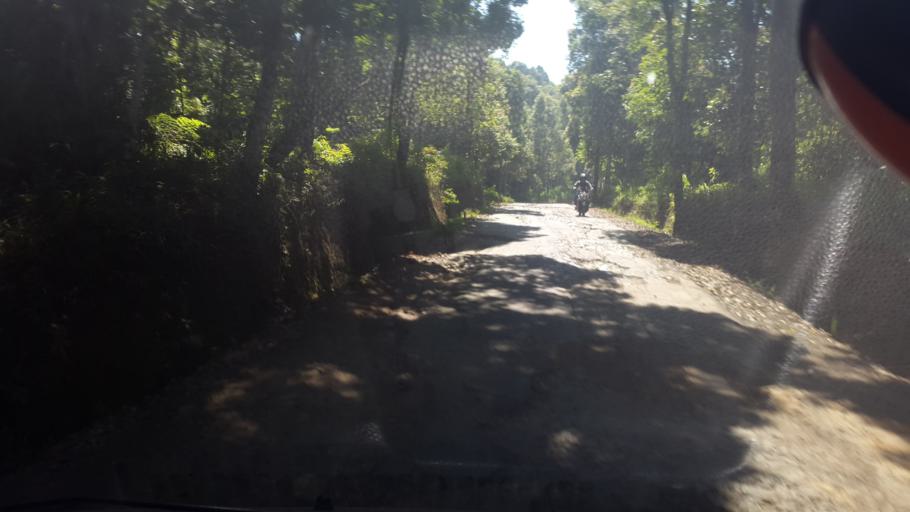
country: ID
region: Banten
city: Kubang
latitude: -6.7571
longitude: 106.6127
